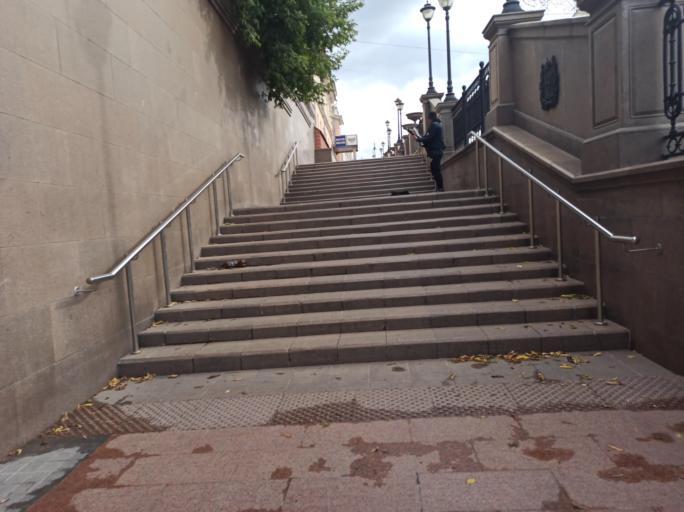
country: RU
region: Tomsk
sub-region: Tomskiy Rayon
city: Tomsk
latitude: 56.4812
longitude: 84.9496
